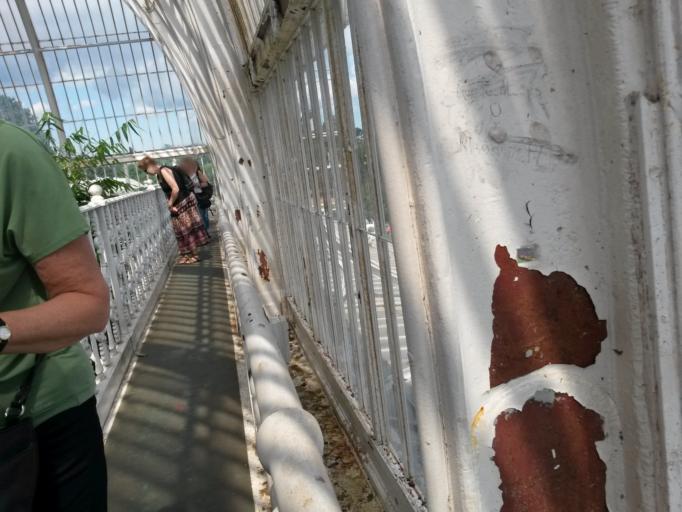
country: GB
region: England
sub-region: Greater London
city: Brentford
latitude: 51.4790
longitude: -0.2927
